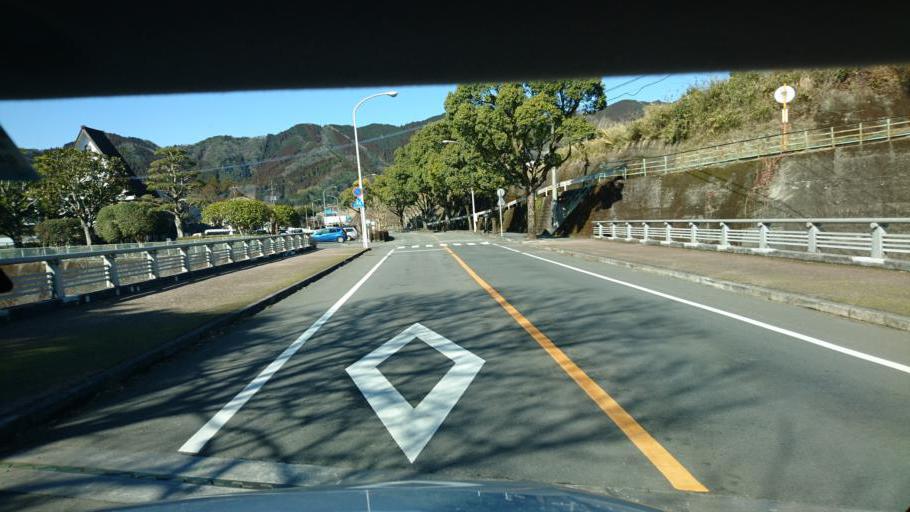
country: JP
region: Oita
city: Takedamachi
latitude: 32.7143
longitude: 131.3075
